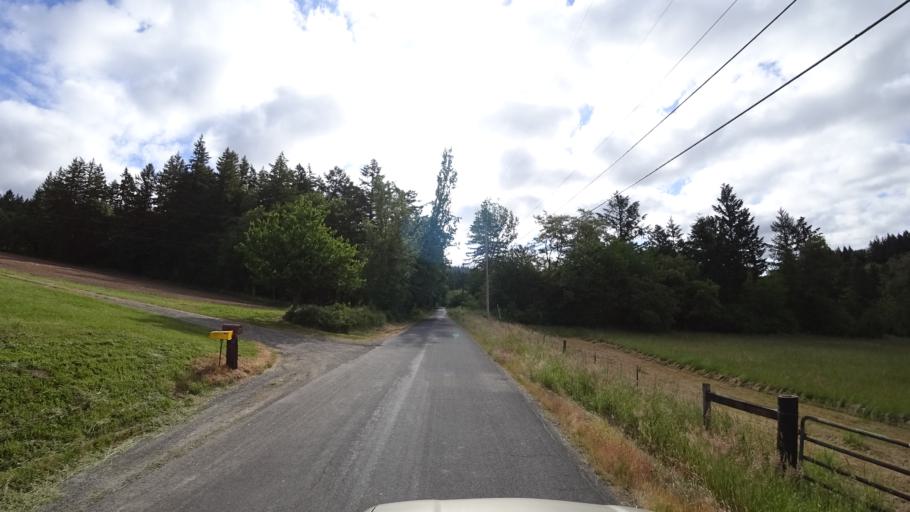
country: US
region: Oregon
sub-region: Washington County
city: Oak Hills
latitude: 45.5811
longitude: -122.8282
